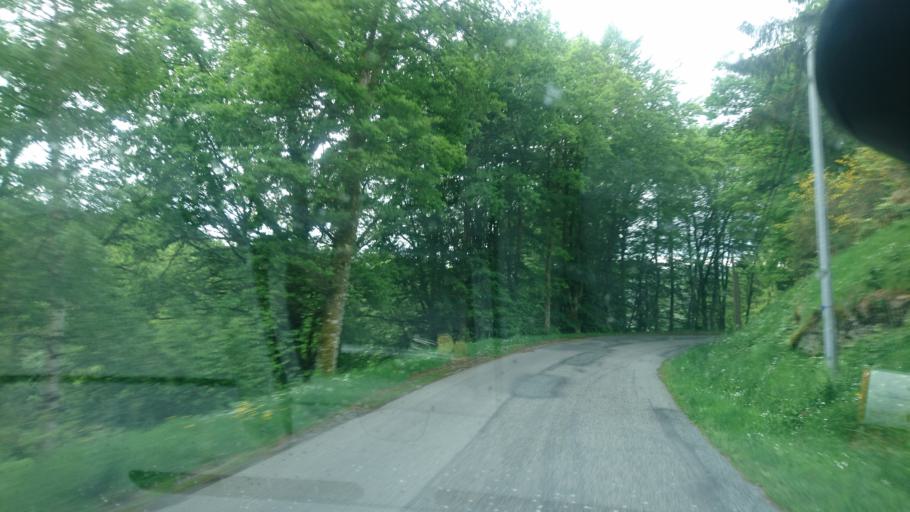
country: FR
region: Limousin
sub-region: Departement de la Haute-Vienne
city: Peyrat-le-Chateau
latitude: 45.8311
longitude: 1.8775
